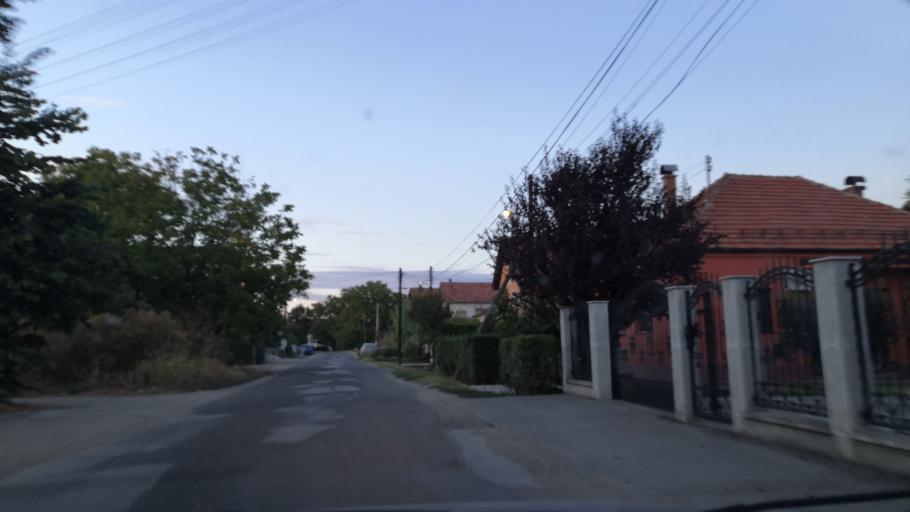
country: RS
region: Central Serbia
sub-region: Borski Okrug
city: Negotin
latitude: 44.2368
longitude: 22.5290
